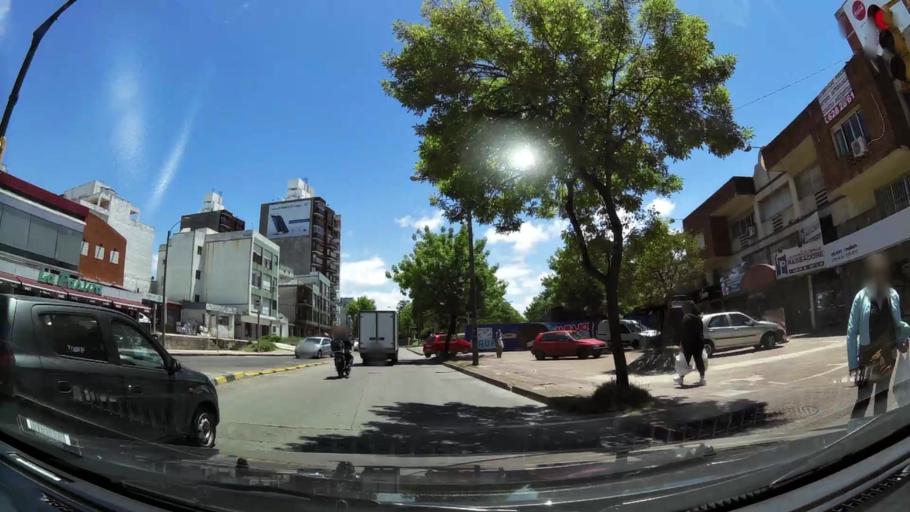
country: UY
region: Montevideo
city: Montevideo
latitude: -34.9011
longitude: -56.1385
